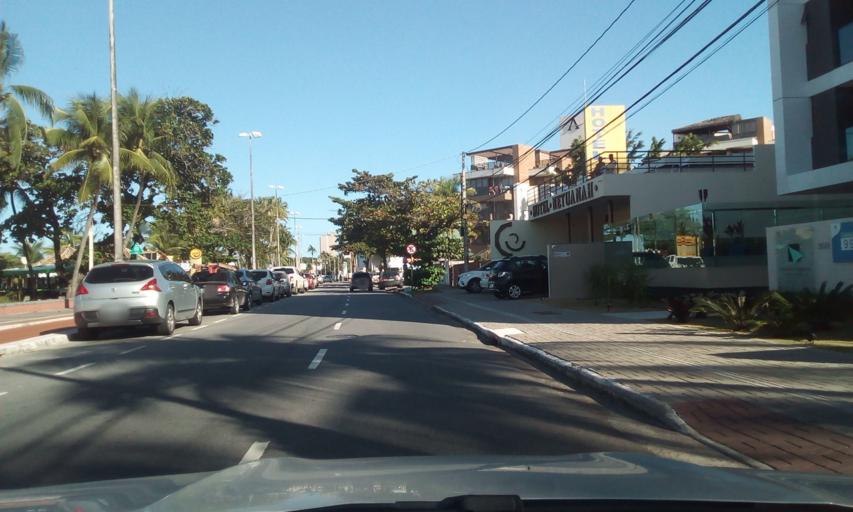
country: BR
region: Paraiba
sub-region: Joao Pessoa
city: Joao Pessoa
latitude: -7.1332
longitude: -34.8212
